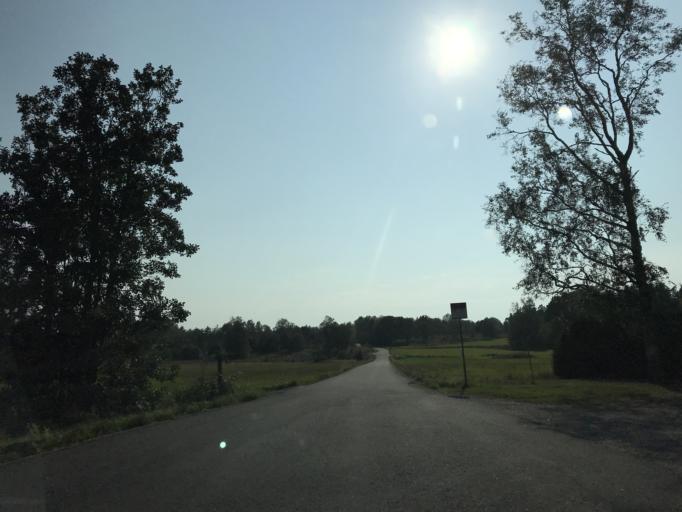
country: SE
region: Stockholm
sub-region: Norrtalje Kommun
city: Bjorko
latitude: 59.8545
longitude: 19.0177
